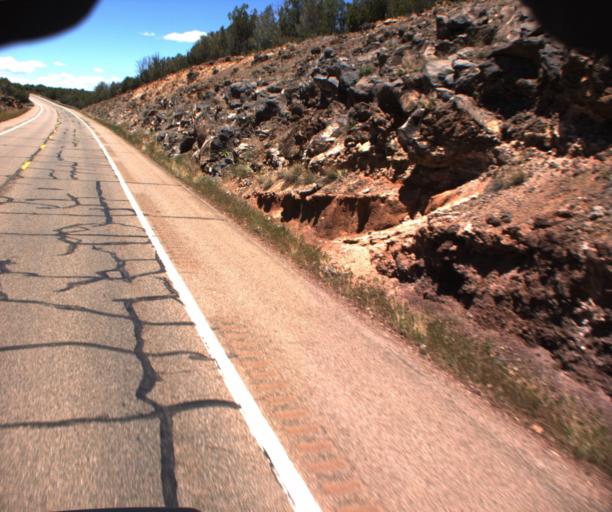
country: US
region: Arizona
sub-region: Yavapai County
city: Paulden
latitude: 35.0830
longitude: -112.4063
